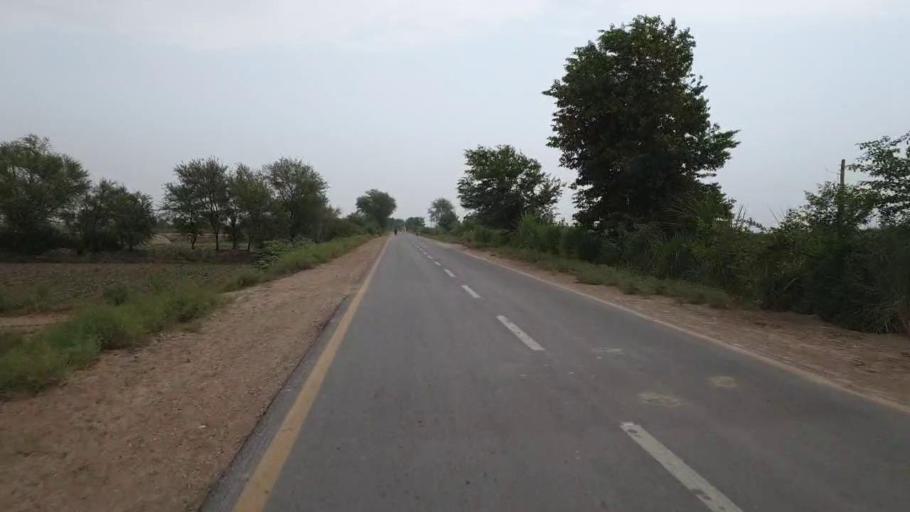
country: PK
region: Sindh
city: Bandhi
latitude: 26.5895
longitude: 68.2125
